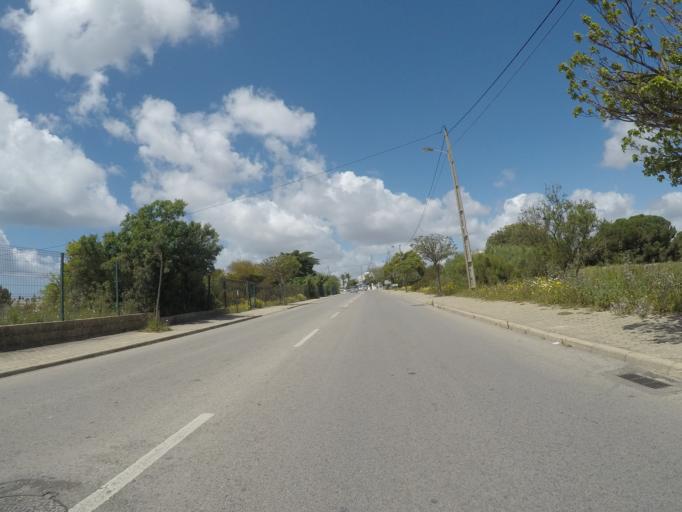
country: PT
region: Faro
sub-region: Silves
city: Armacao de Pera
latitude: 37.1054
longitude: -8.3781
